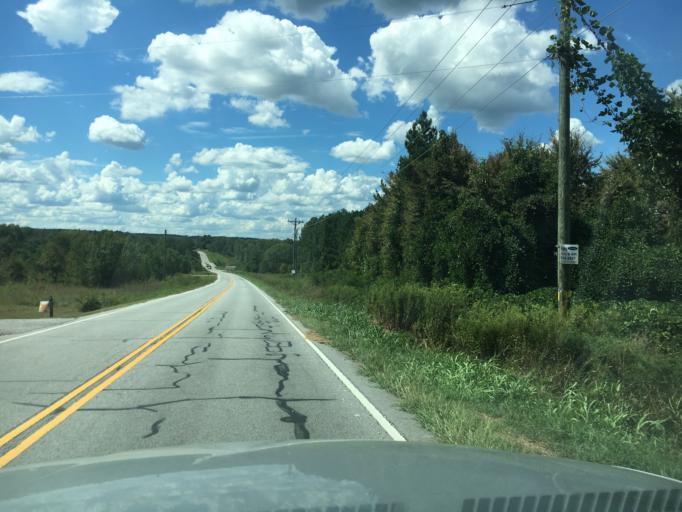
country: US
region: South Carolina
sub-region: Laurens County
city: Laurens
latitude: 34.5247
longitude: -82.1220
